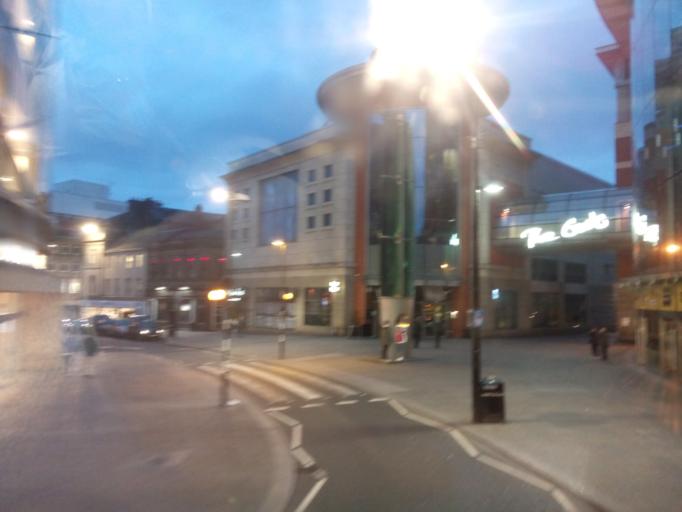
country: GB
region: England
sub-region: Newcastle upon Tyne
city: Newcastle upon Tyne
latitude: 54.9730
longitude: -1.6173
